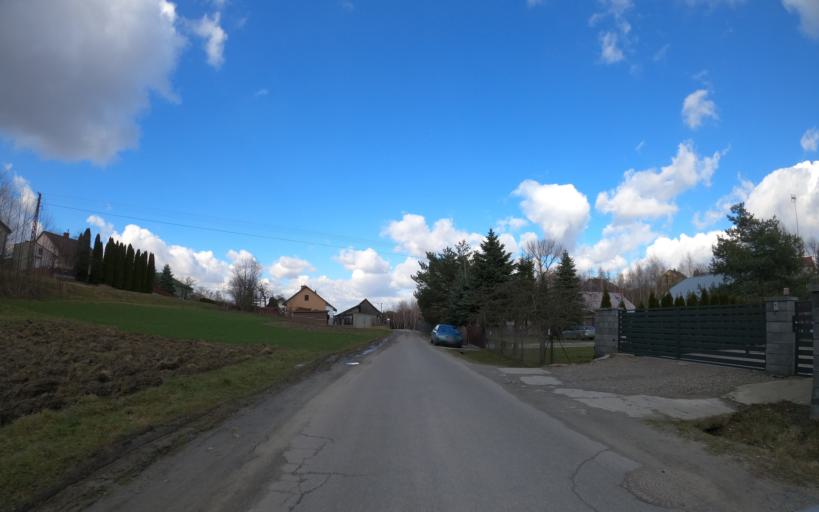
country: PL
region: Subcarpathian Voivodeship
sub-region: Powiat debicki
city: Debica
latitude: 50.0359
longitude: 21.4353
